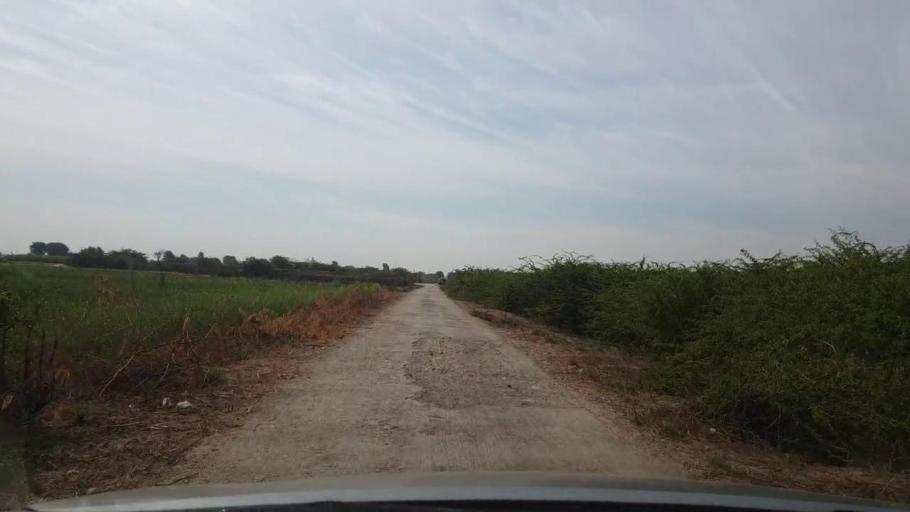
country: PK
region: Sindh
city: Kunri
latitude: 25.1577
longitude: 69.6024
